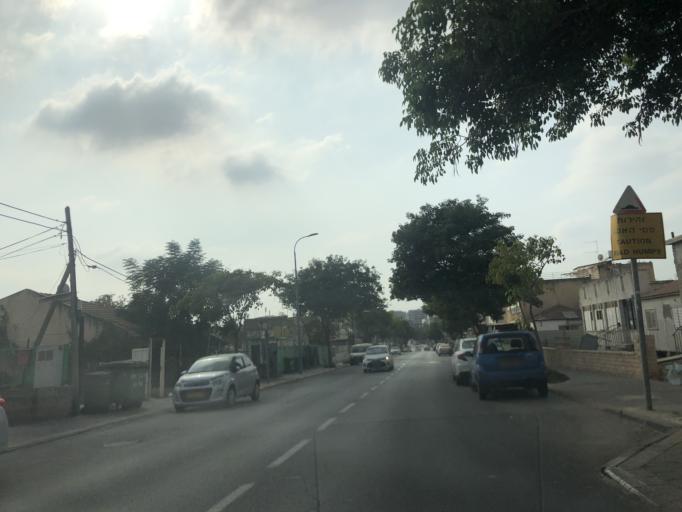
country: IL
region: Central District
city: Rosh Ha'Ayin
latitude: 32.1002
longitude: 34.9484
